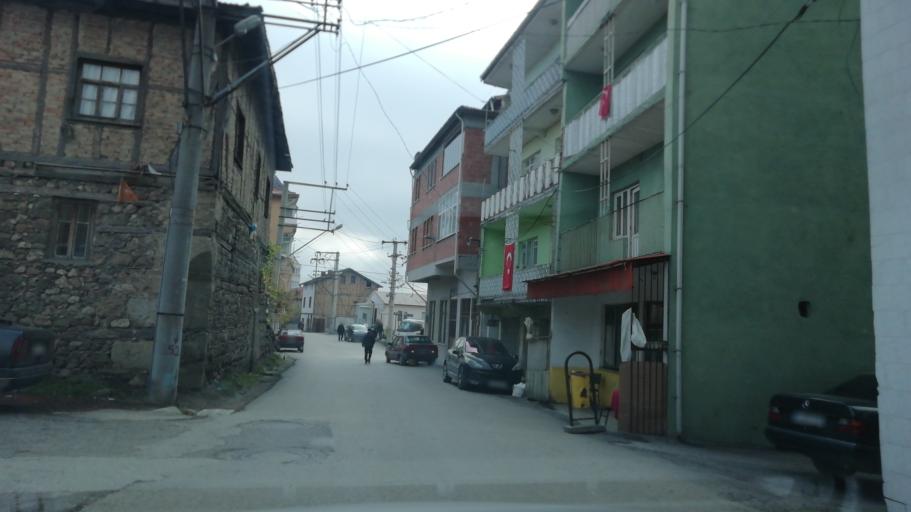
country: TR
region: Karabuk
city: Karabuk
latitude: 41.2206
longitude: 32.6278
